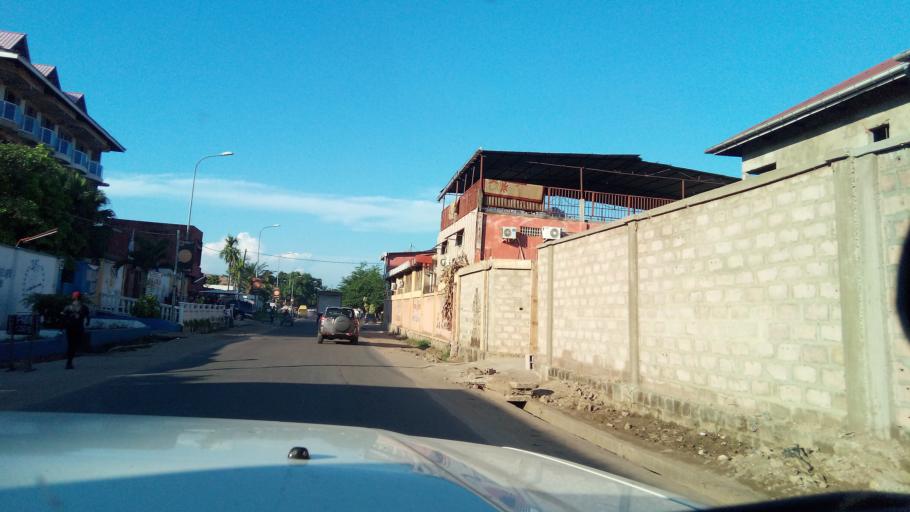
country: CD
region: Kinshasa
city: Kinshasa
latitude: -4.3511
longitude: 15.2642
